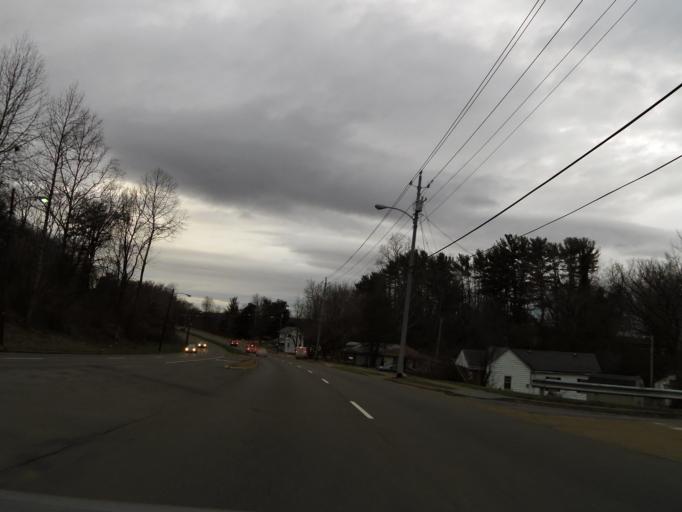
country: US
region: Tennessee
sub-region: Washington County
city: Johnson City
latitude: 36.3026
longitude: -82.3560
